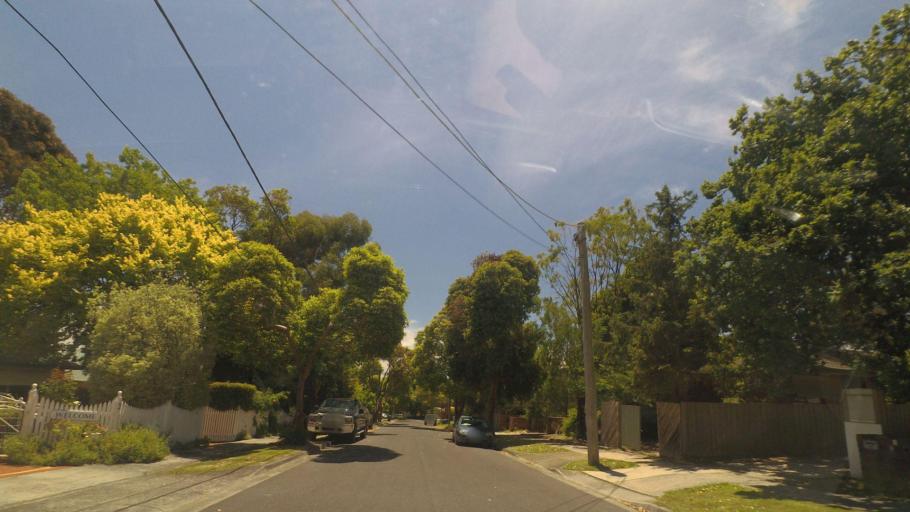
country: AU
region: Victoria
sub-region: Knox
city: Boronia
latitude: -37.8620
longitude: 145.2973
